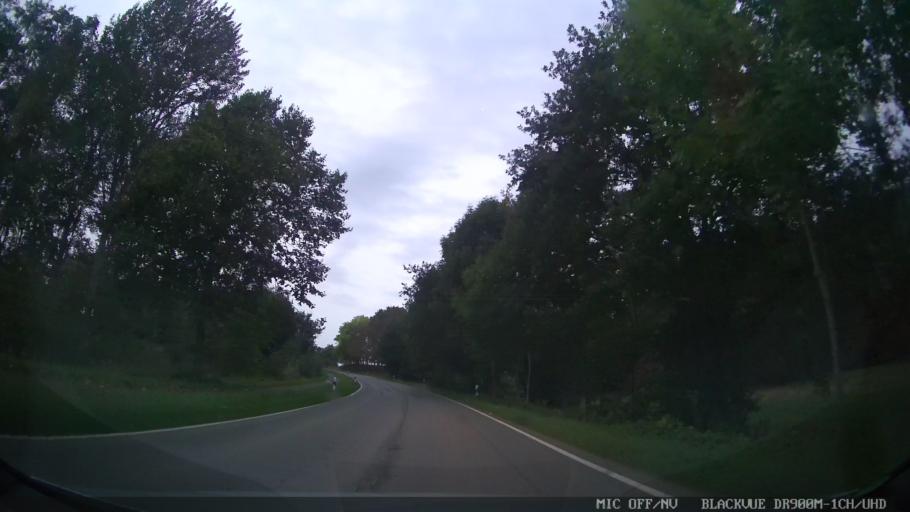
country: DE
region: Schleswig-Holstein
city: Grube
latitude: 54.2664
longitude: 11.0456
